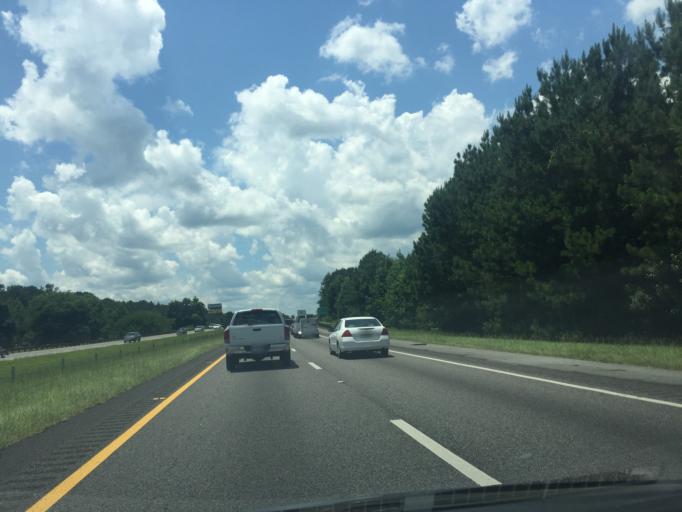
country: US
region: South Carolina
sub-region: Jasper County
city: Hardeeville
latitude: 32.2539
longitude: -81.1102
